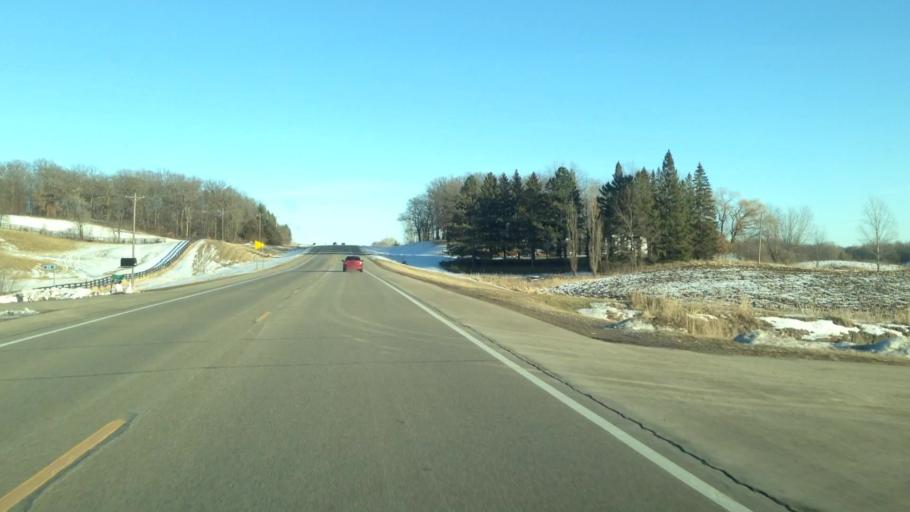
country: US
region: Minnesota
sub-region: Rice County
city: Lonsdale
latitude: 44.4791
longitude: -93.3667
